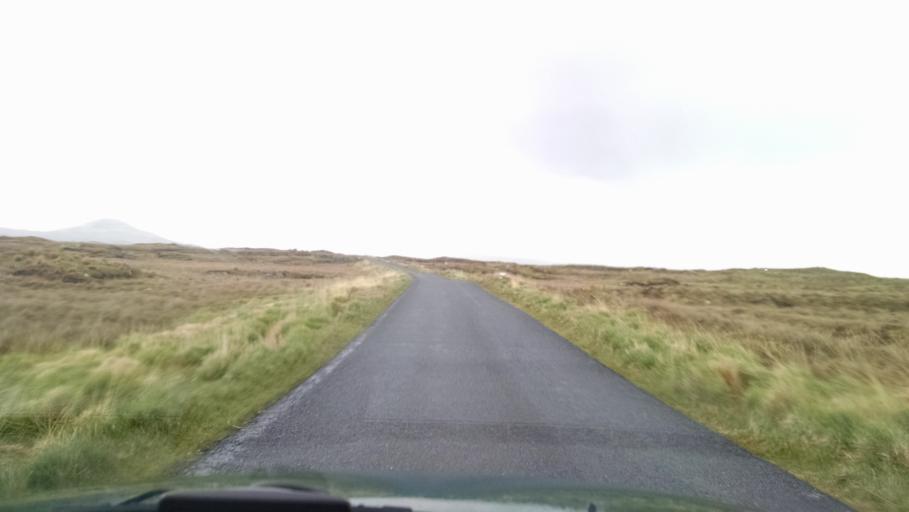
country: IE
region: Connaught
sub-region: County Galway
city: Clifden
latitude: 53.4379
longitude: -9.9163
